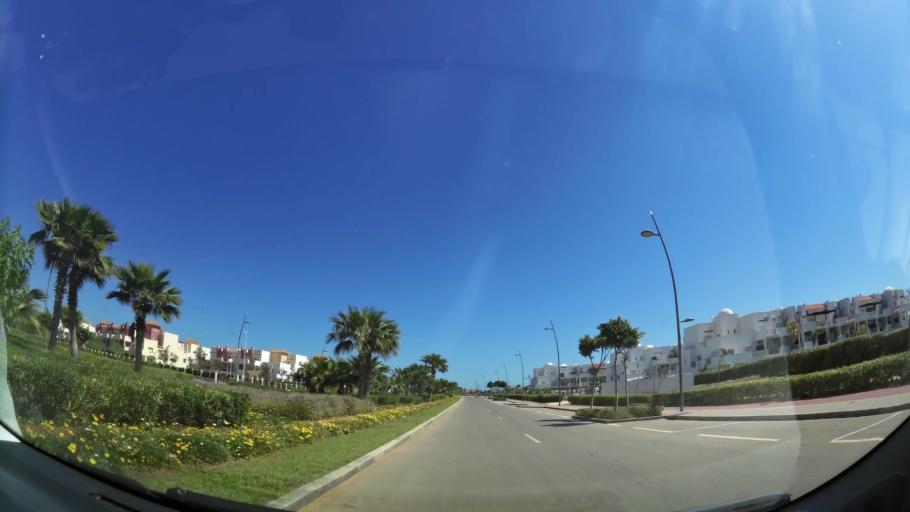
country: MA
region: Oriental
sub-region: Berkane-Taourirt
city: Madagh
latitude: 35.0977
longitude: -2.3007
